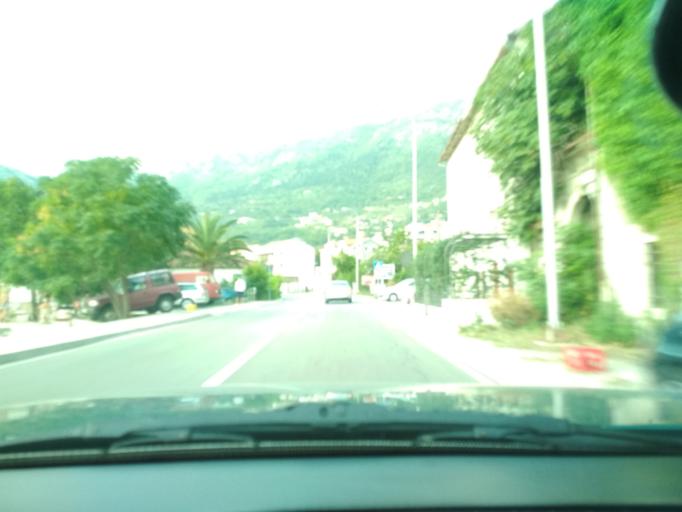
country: ME
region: Kotor
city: Risan
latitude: 42.5084
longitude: 18.6961
